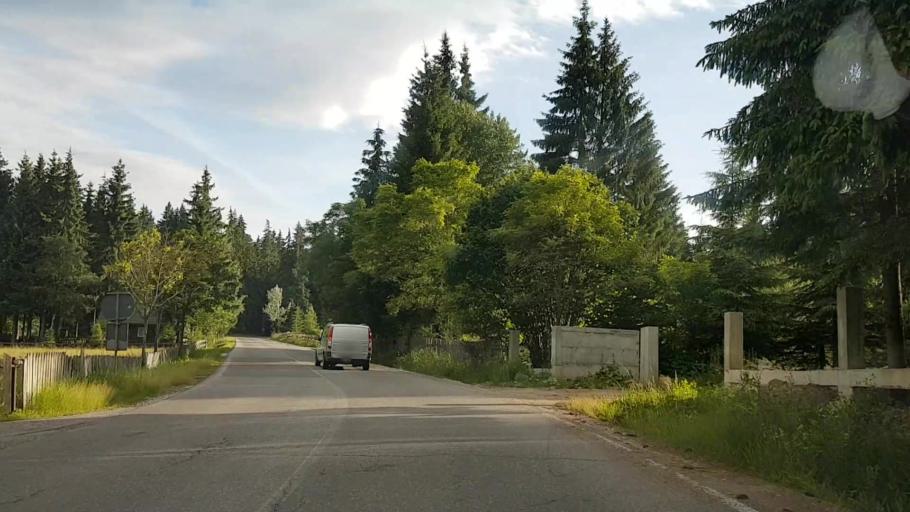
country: RO
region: Harghita
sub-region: Comuna Remetea
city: Remetea
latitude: 46.6754
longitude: 25.3611
